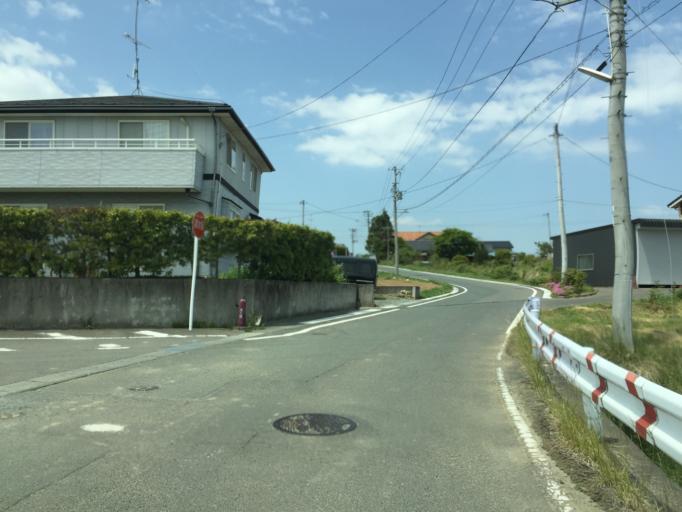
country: JP
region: Miyagi
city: Marumori
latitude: 37.8731
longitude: 140.9209
